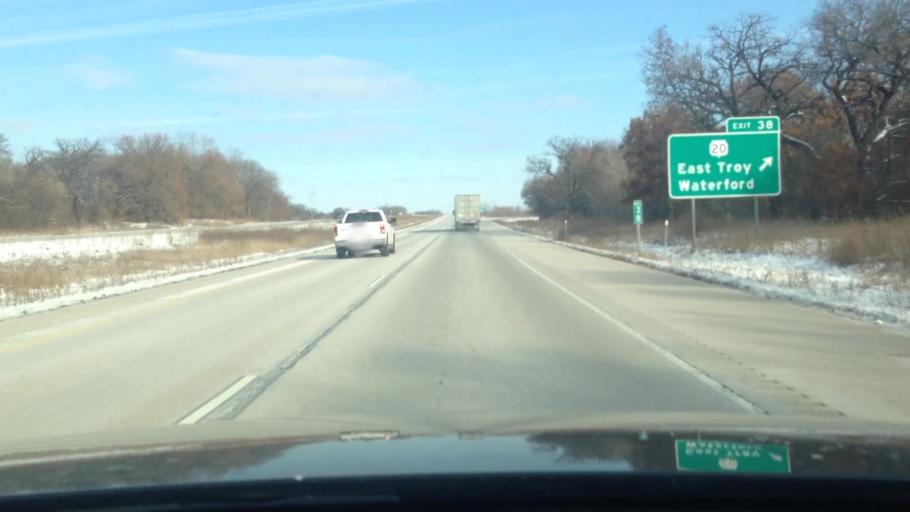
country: US
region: Wisconsin
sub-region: Walworth County
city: East Troy
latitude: 42.7850
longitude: -88.3881
